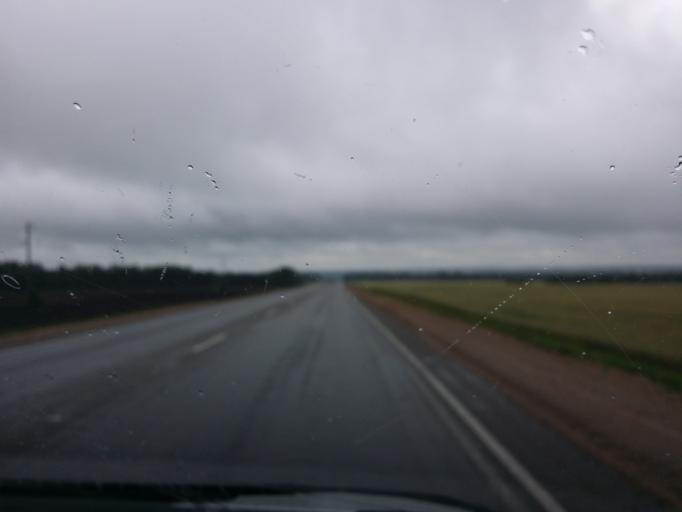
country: RU
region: Altai Krai
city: Nalobikha
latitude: 53.2408
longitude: 84.5934
